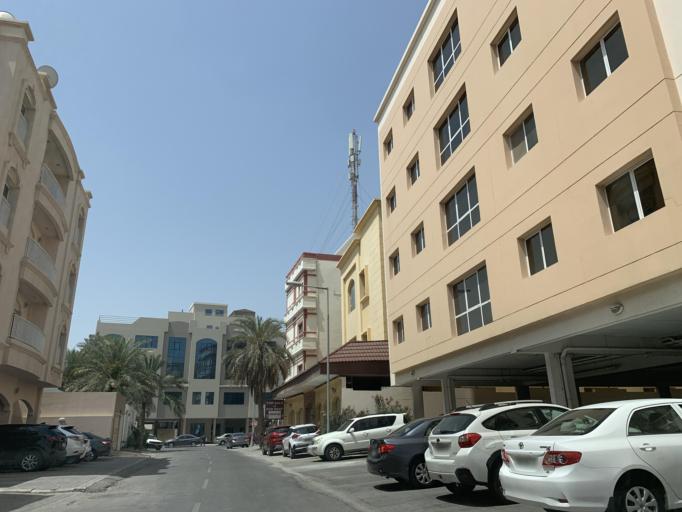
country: BH
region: Manama
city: Jidd Hafs
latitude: 26.2024
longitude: 50.5641
